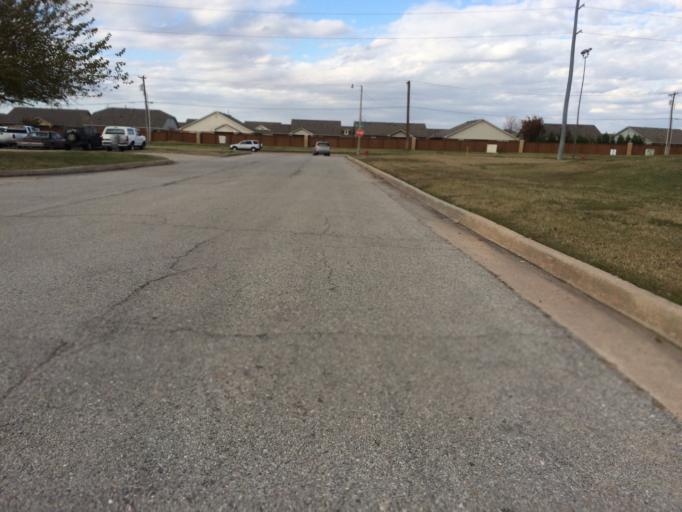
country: US
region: Oklahoma
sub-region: Cleveland County
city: Norman
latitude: 35.2466
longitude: -97.4528
